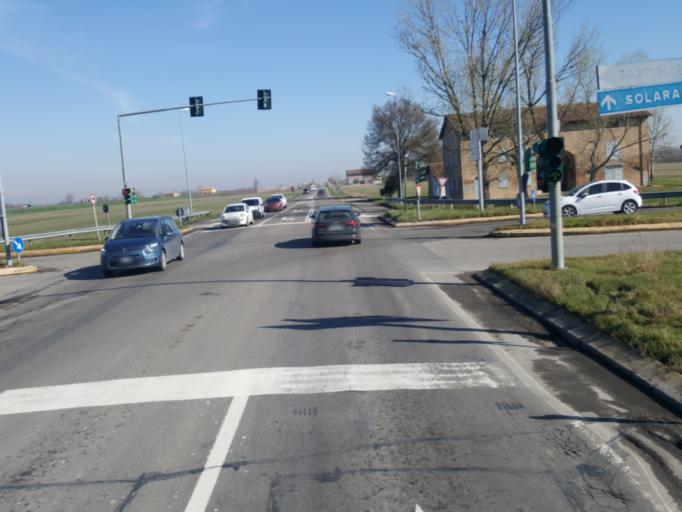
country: IT
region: Emilia-Romagna
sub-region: Provincia di Modena
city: Bomporto
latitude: 44.7138
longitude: 11.0225
